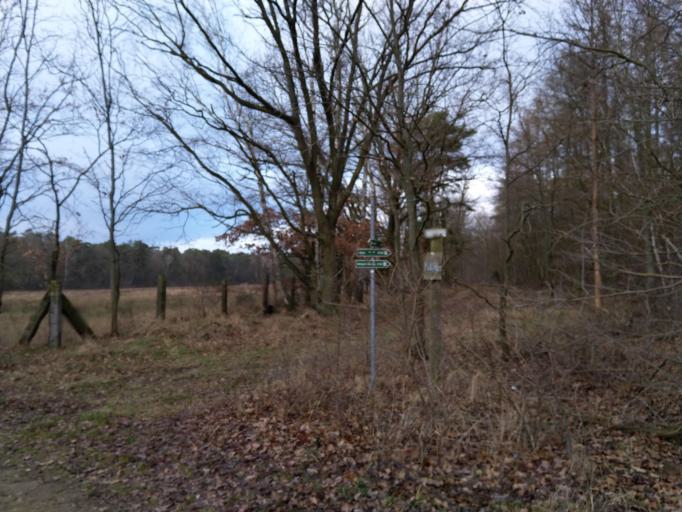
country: DE
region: Brandenburg
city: Bernau bei Berlin
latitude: 52.6269
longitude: 13.6277
